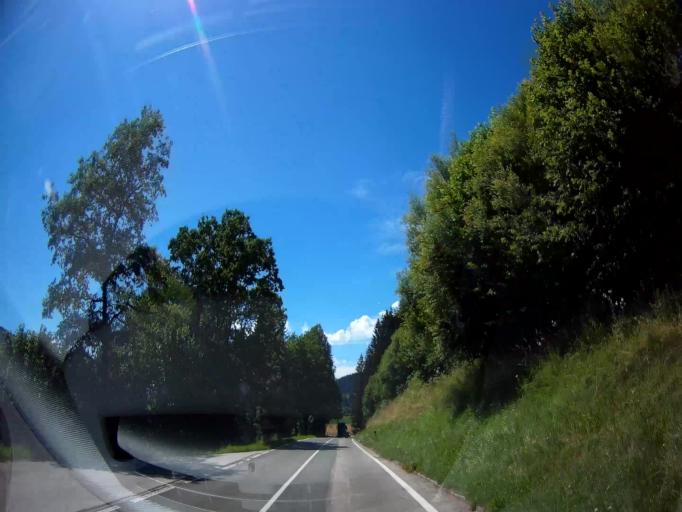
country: AT
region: Carinthia
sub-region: Politischer Bezirk Sankt Veit an der Glan
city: Glodnitz
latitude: 46.8523
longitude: 14.1850
